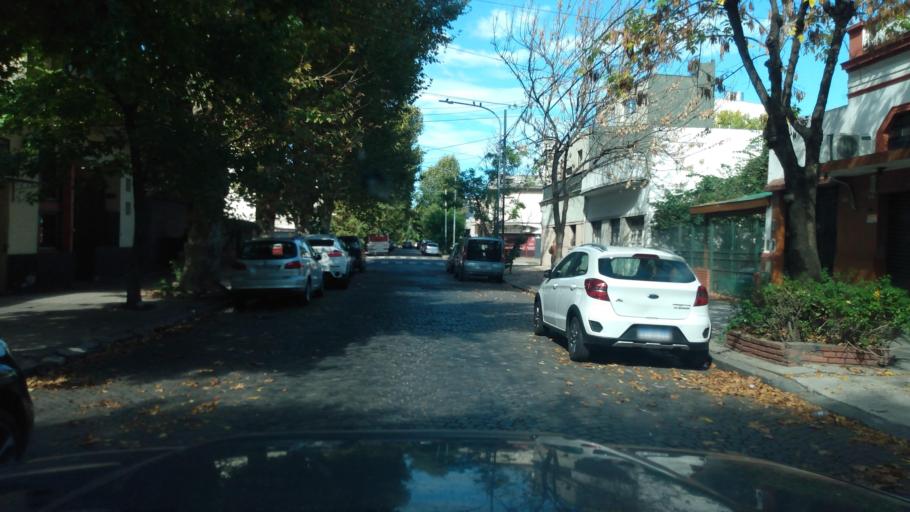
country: AR
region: Buenos Aires
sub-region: Partido de General San Martin
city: General San Martin
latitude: -34.5656
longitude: -58.4984
